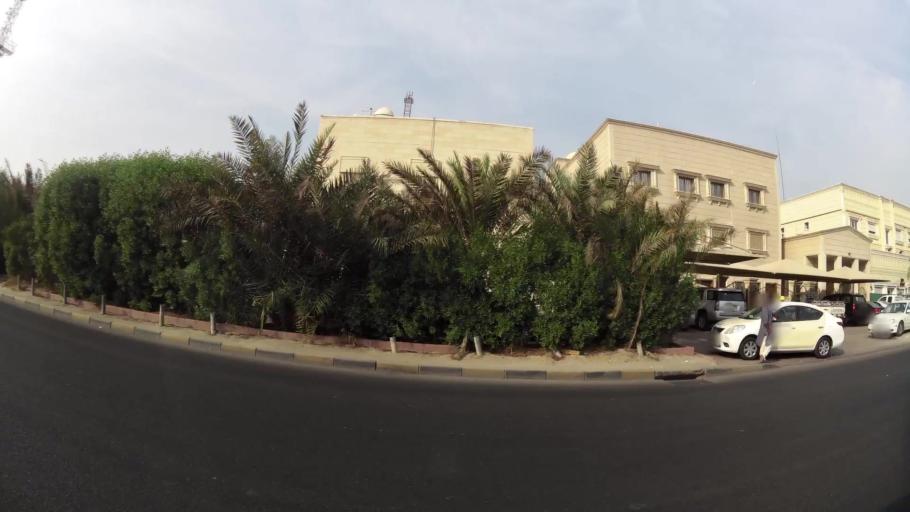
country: KW
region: Al Farwaniyah
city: Janub as Surrah
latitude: 29.2834
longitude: 47.9816
